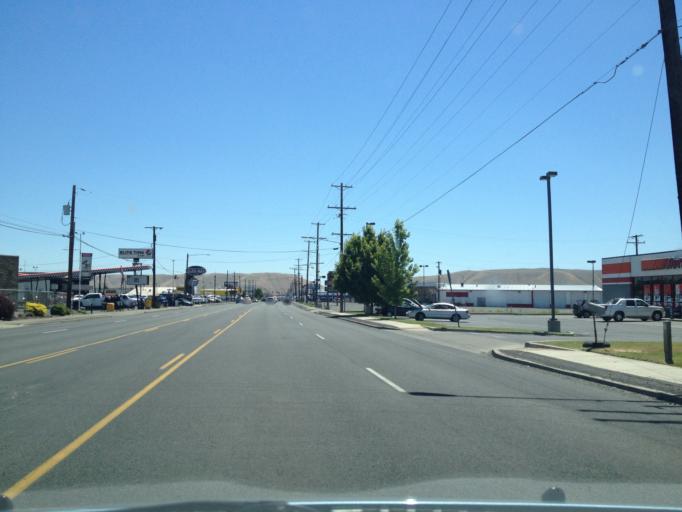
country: US
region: Washington
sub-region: Yakima County
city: Yakima
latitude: 46.5824
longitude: -120.4949
